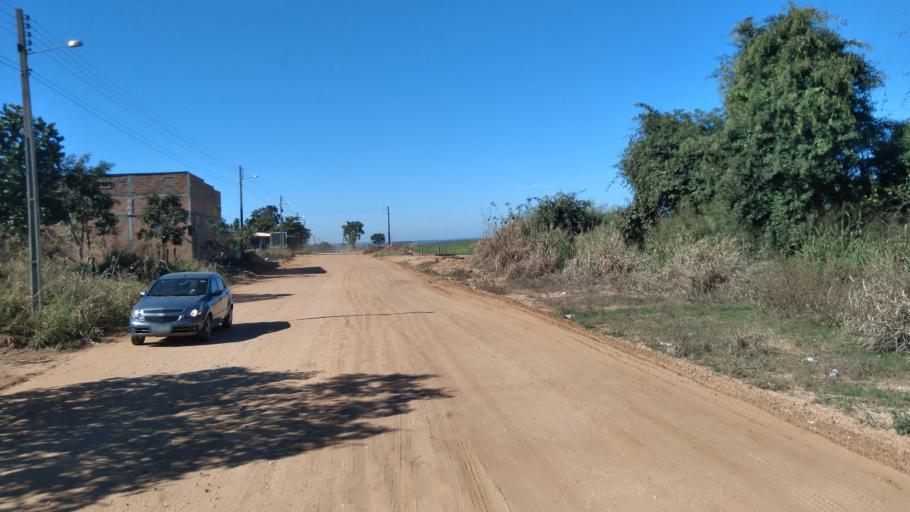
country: BR
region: Goias
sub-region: Mineiros
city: Mineiros
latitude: -17.5925
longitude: -52.5582
